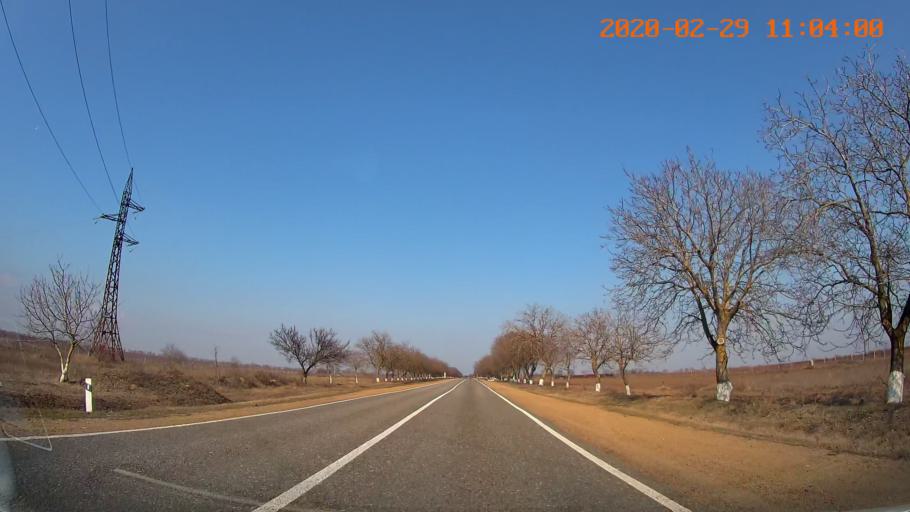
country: MD
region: Criuleni
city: Criuleni
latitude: 47.1835
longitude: 29.2074
